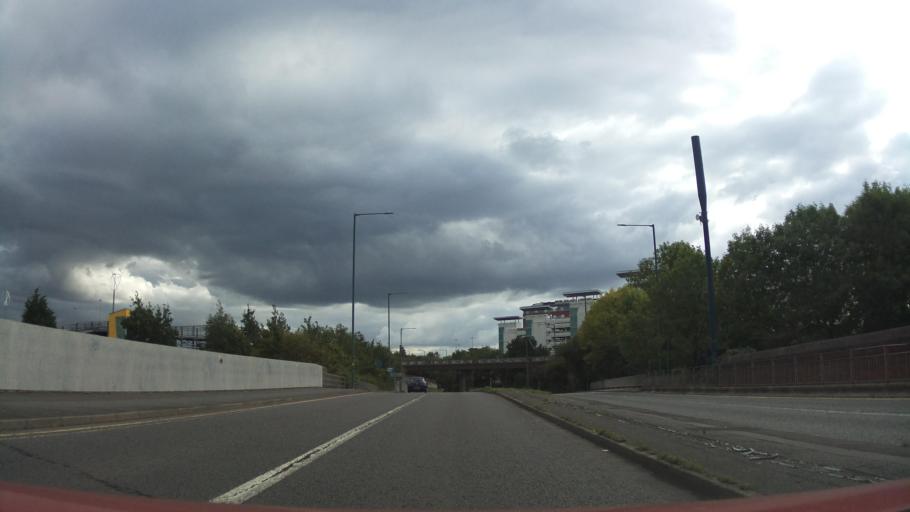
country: GB
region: England
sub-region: Solihull
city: Bickenhill
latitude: 52.4532
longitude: -1.7278
